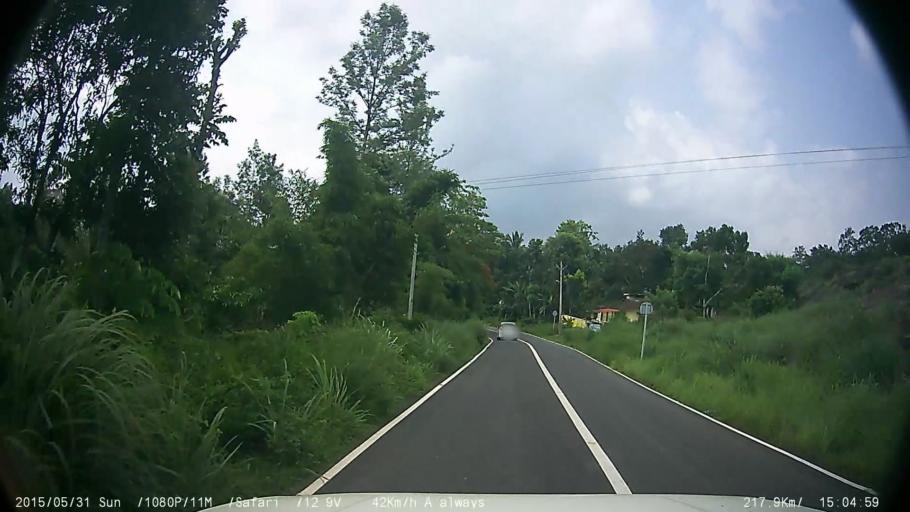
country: IN
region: Kerala
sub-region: Wayanad
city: Kalpetta
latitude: 11.6363
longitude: 76.2128
